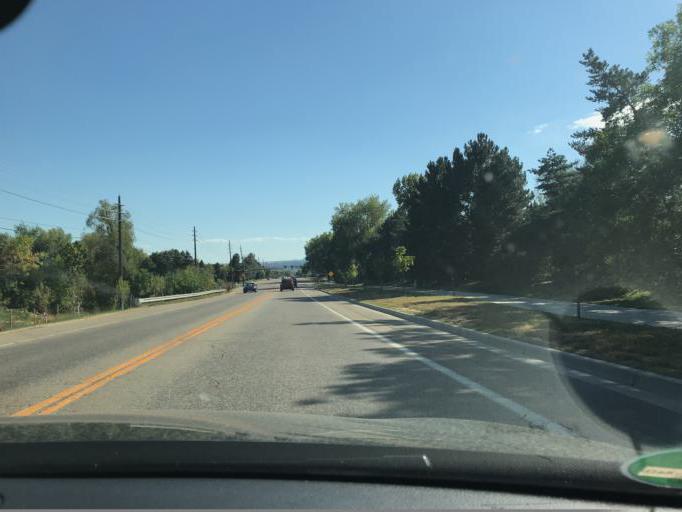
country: US
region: Colorado
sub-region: Boulder County
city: Boulder
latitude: 40.0420
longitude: -105.2585
